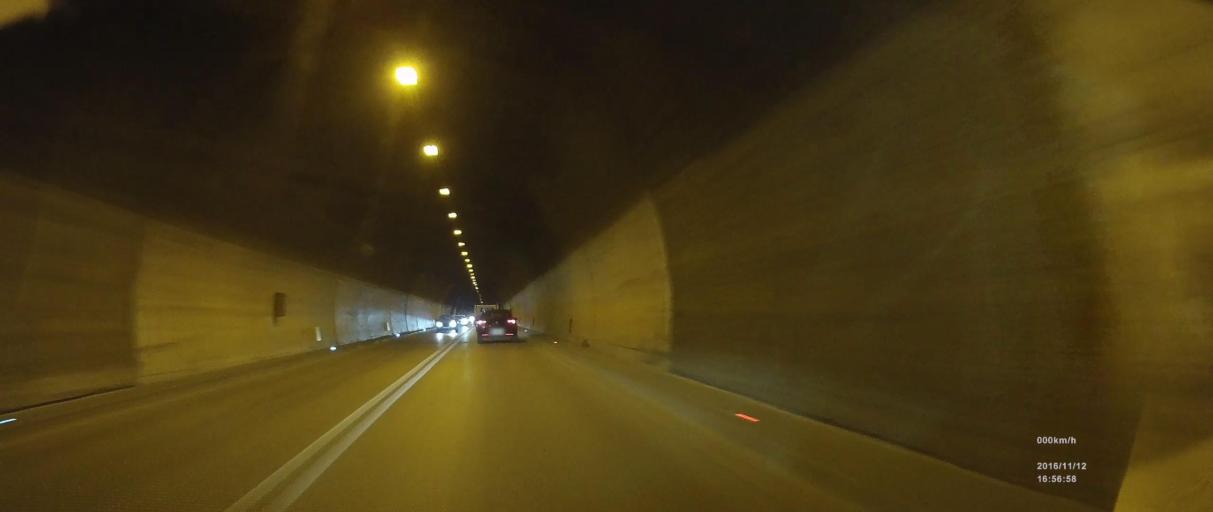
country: HR
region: Splitsko-Dalmatinska
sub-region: Grad Split
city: Split
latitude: 43.5080
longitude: 16.4252
